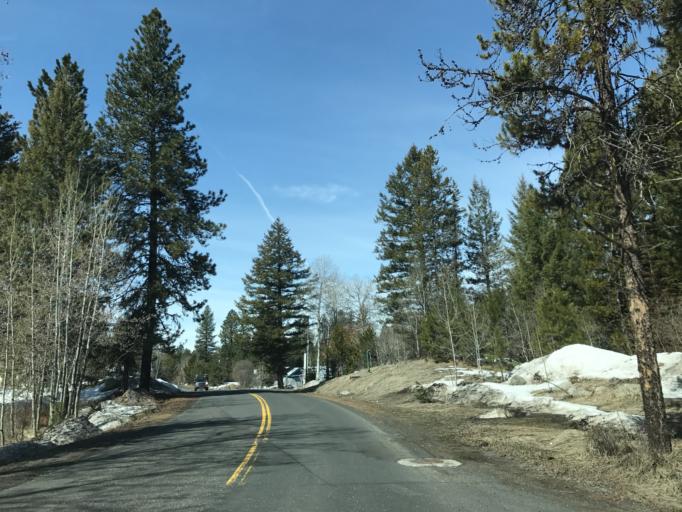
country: US
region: Idaho
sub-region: Valley County
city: McCall
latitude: 44.9121
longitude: -116.0844
